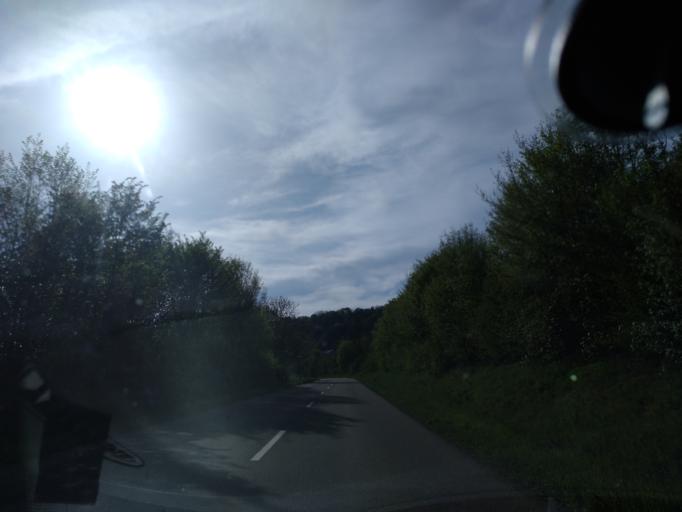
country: DE
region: Baden-Wuerttemberg
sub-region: Regierungsbezirk Stuttgart
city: Untermunkheim
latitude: 49.1613
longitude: 9.7639
